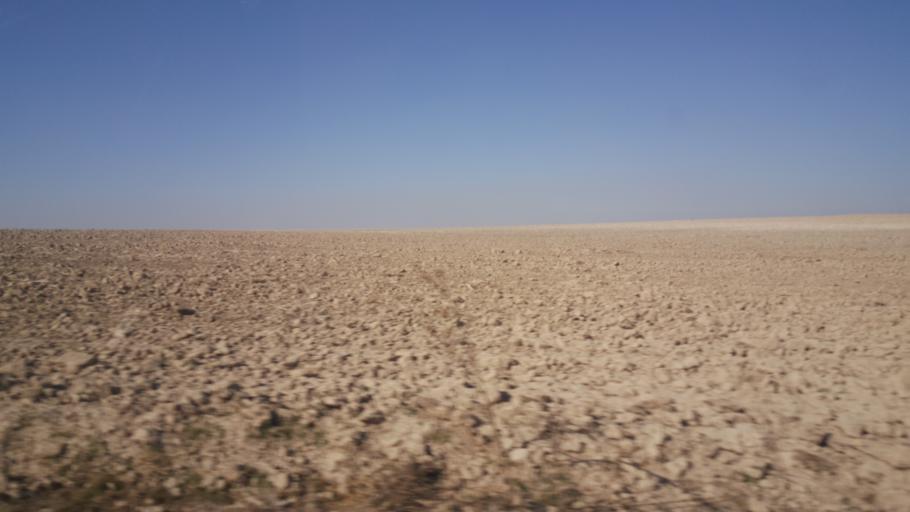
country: TR
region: Konya
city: Celtik
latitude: 39.0616
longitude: 31.8720
